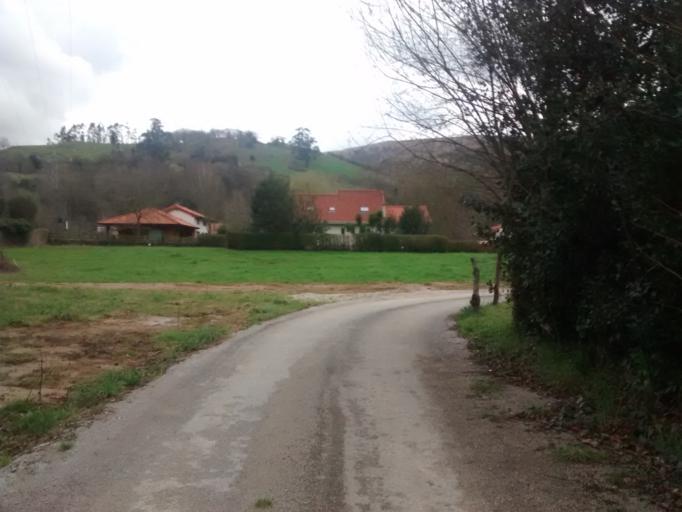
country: ES
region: Cantabria
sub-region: Provincia de Cantabria
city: Entrambasaguas
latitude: 43.3433
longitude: -3.6820
